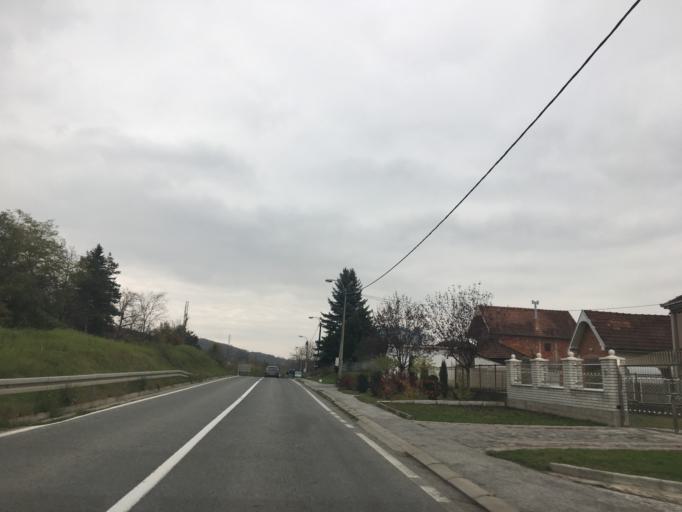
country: RS
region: Central Serbia
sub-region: Raski Okrug
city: Kraljevo
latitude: 43.7279
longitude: 20.7547
